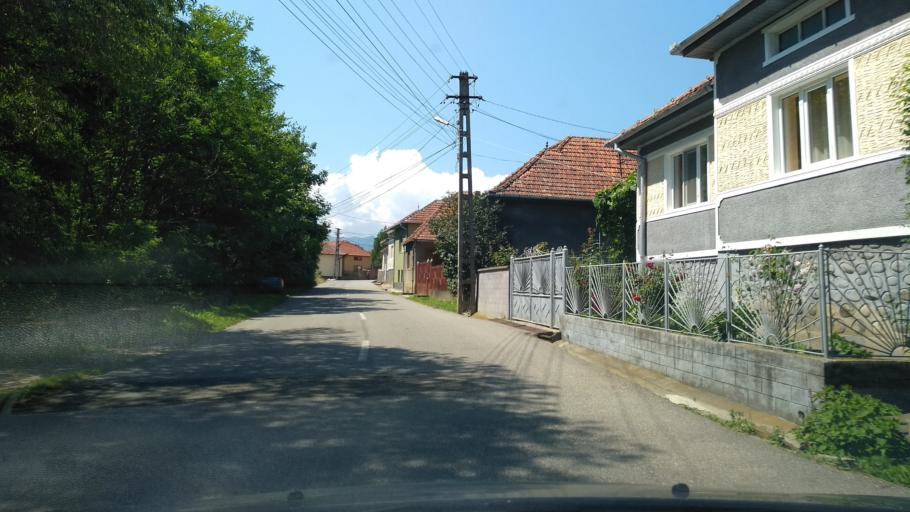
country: RO
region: Hunedoara
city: Salasu de Sus
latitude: 45.5345
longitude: 22.9739
